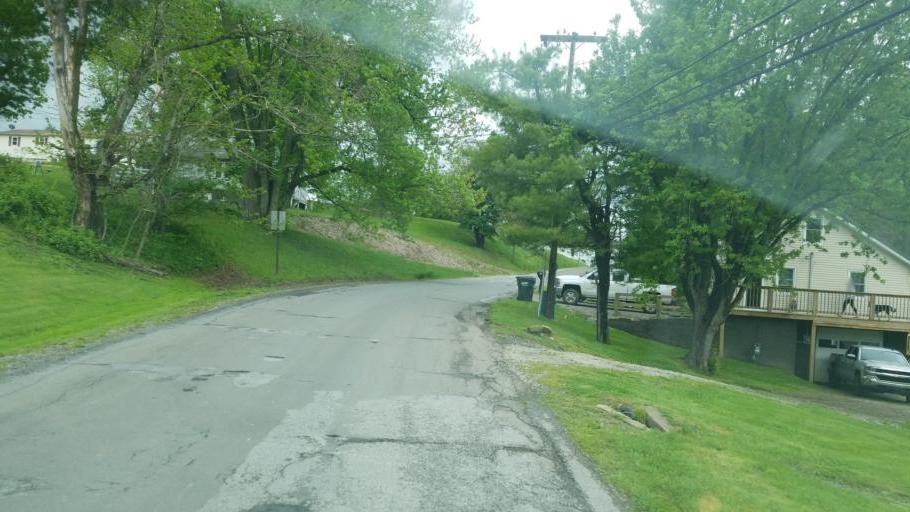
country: US
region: Ohio
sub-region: Harrison County
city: Cadiz
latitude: 40.2713
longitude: -80.9846
